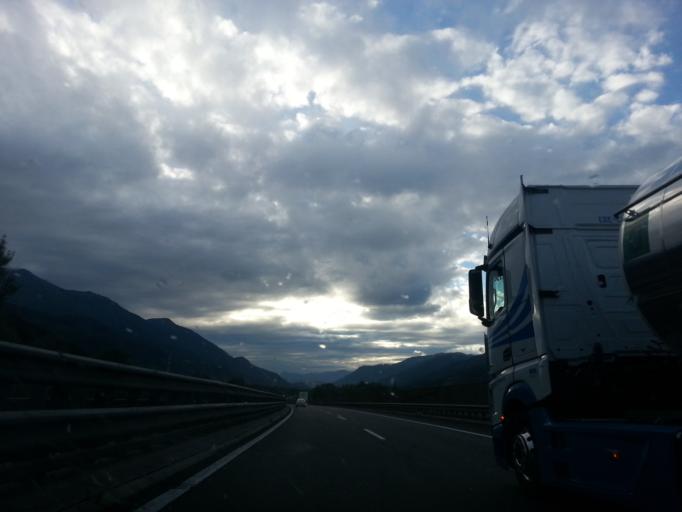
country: AT
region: Styria
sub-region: Politischer Bezirk Liezen
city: Trieben
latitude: 47.4861
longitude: 14.5270
